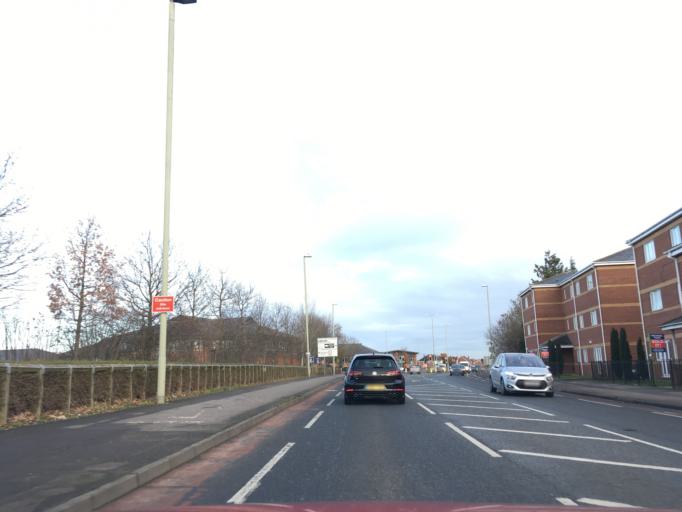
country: GB
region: England
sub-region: Gloucestershire
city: Gloucester
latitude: 51.8326
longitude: -2.2760
